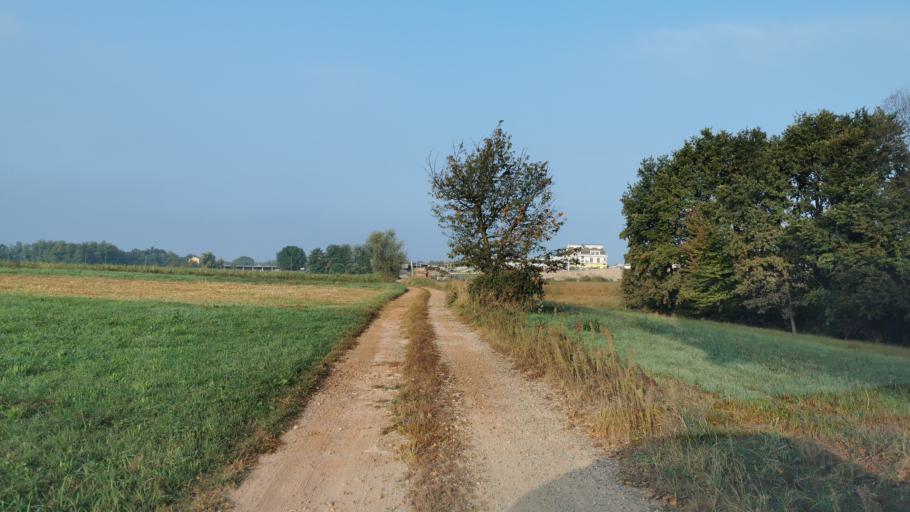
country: IT
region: Piedmont
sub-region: Provincia di Torino
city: Front
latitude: 45.2573
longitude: 7.6660
